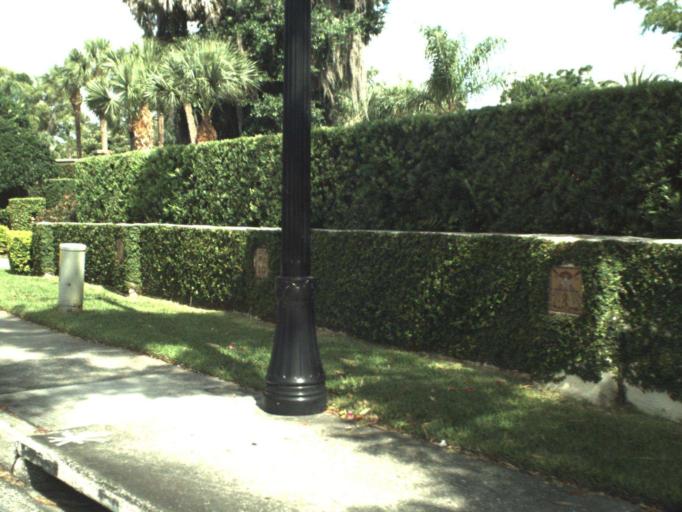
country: US
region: Florida
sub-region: Orange County
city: Winter Park
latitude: 28.5957
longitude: -81.3425
